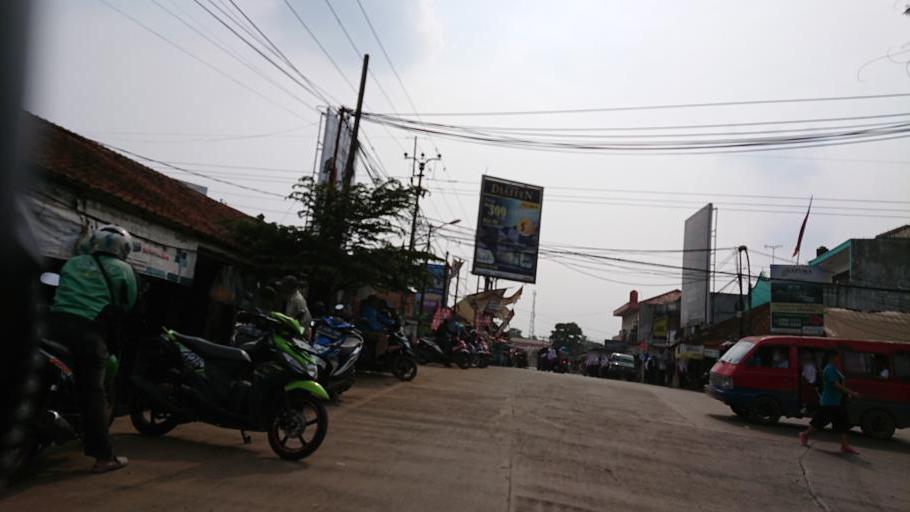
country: ID
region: West Java
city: Parung
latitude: -6.3847
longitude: 106.6807
